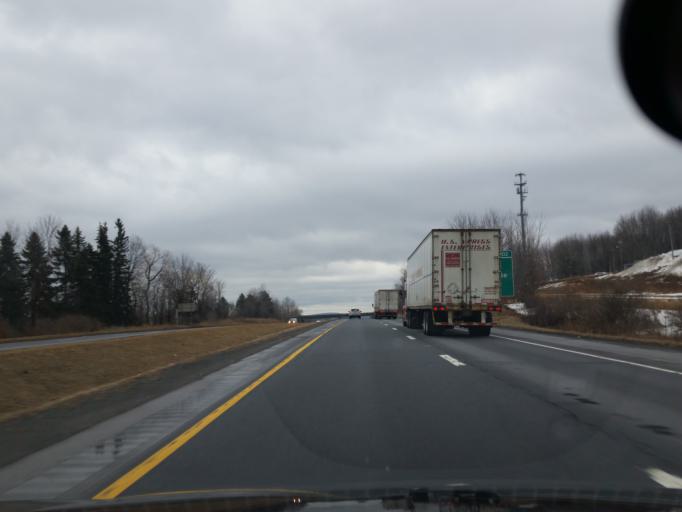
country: US
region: Pennsylvania
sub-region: Lackawanna County
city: Dalton
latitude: 41.6253
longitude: -75.6437
